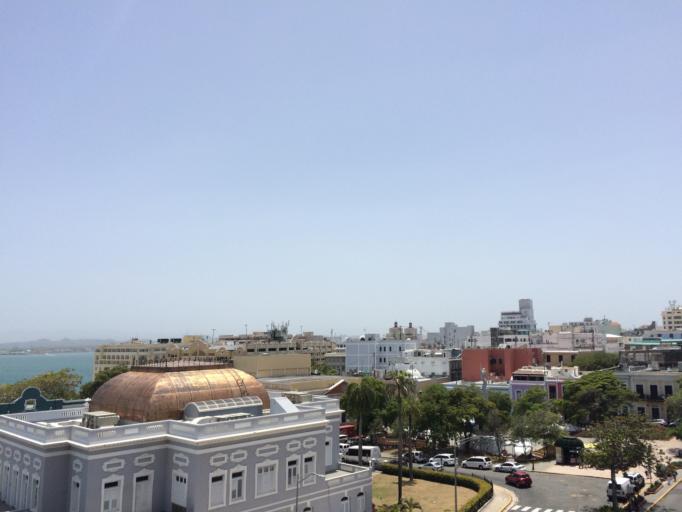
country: PR
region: San Juan
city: San Juan
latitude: 18.4668
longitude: -66.1111
